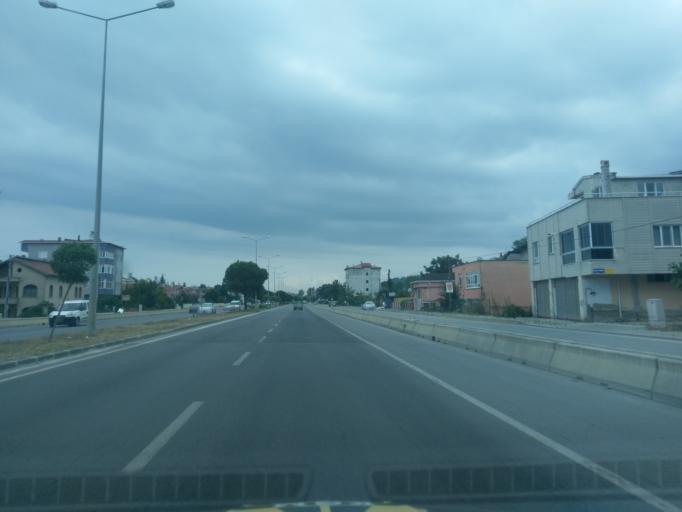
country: TR
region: Samsun
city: Taflan
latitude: 41.3985
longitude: 36.1943
